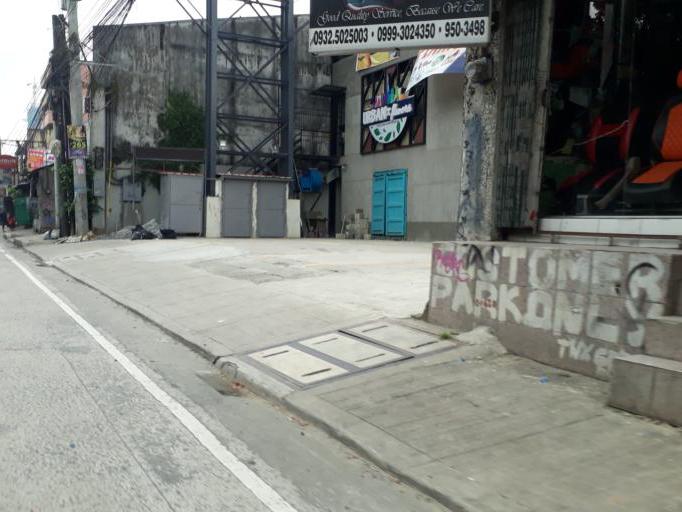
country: PH
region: Calabarzon
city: Bagong Pagasa
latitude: 14.6569
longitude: 121.0356
